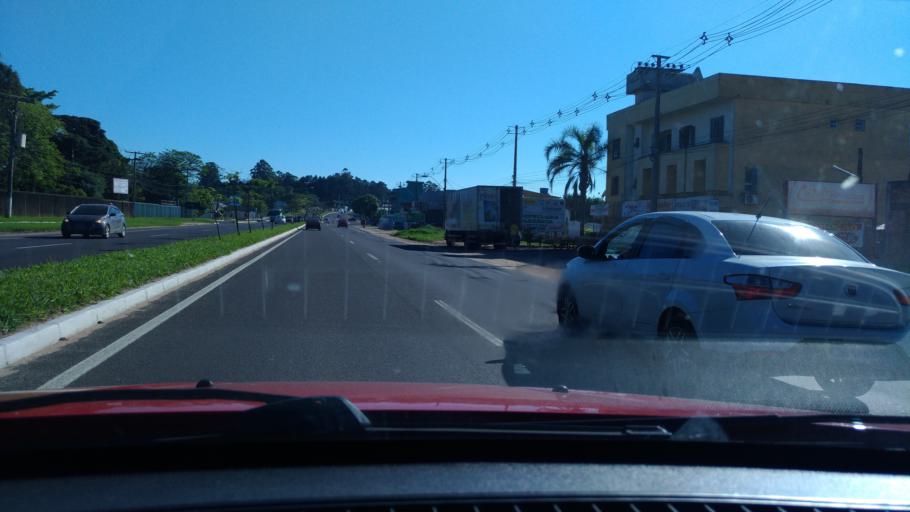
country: BR
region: Rio Grande do Sul
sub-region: Viamao
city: Viamao
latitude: -30.0809
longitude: -51.0520
